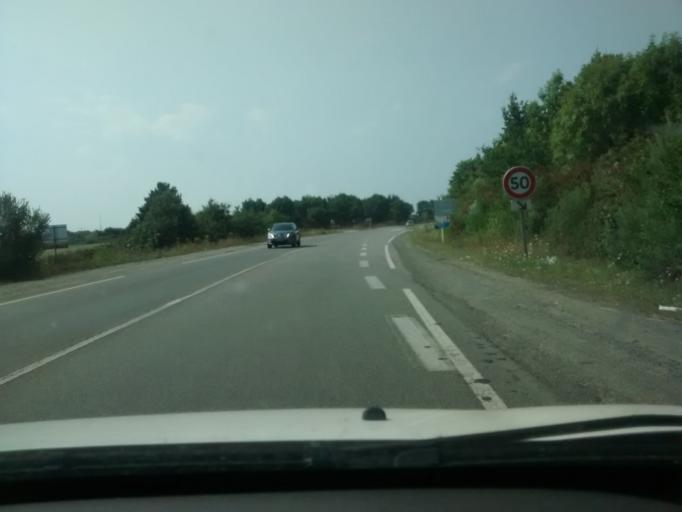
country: FR
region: Pays de la Loire
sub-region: Departement de la Loire-Atlantique
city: Saint-Andre-des-Eaux
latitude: 47.2822
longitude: -2.3018
